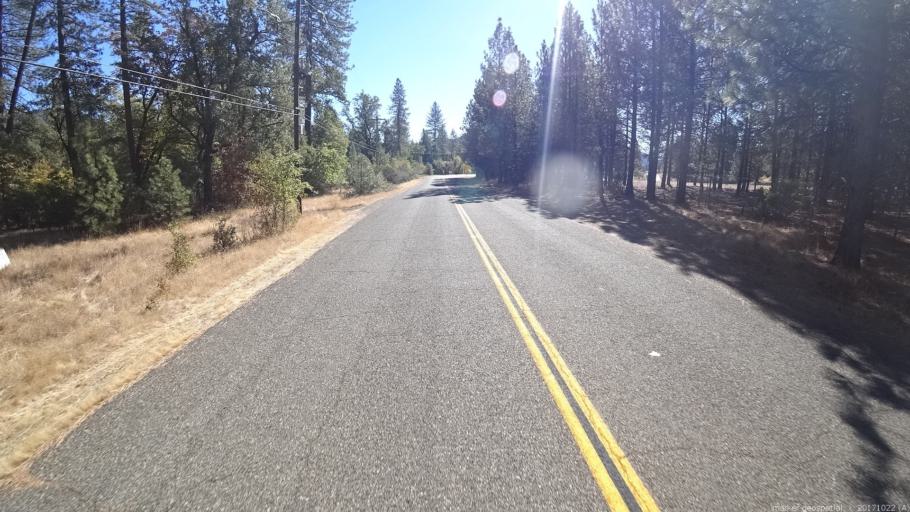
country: US
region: California
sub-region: Shasta County
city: Central Valley (historical)
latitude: 40.8937
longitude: -122.3821
